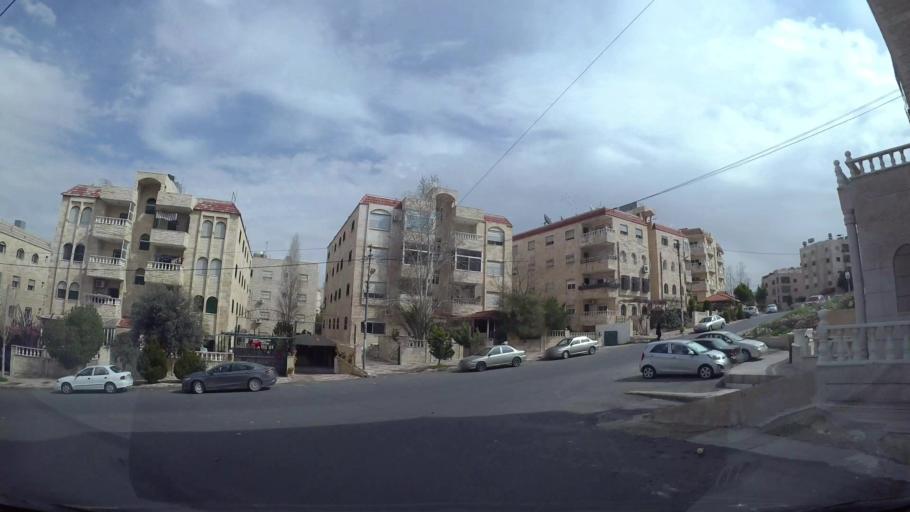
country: JO
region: Amman
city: Amman
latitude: 32.0026
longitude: 35.9353
